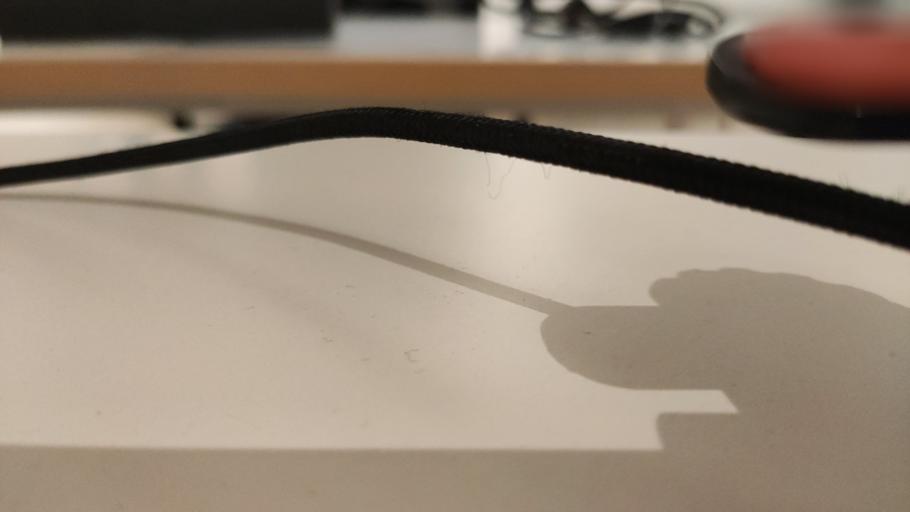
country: RU
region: Moskovskaya
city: Dorokhovo
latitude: 55.4546
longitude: 36.3530
